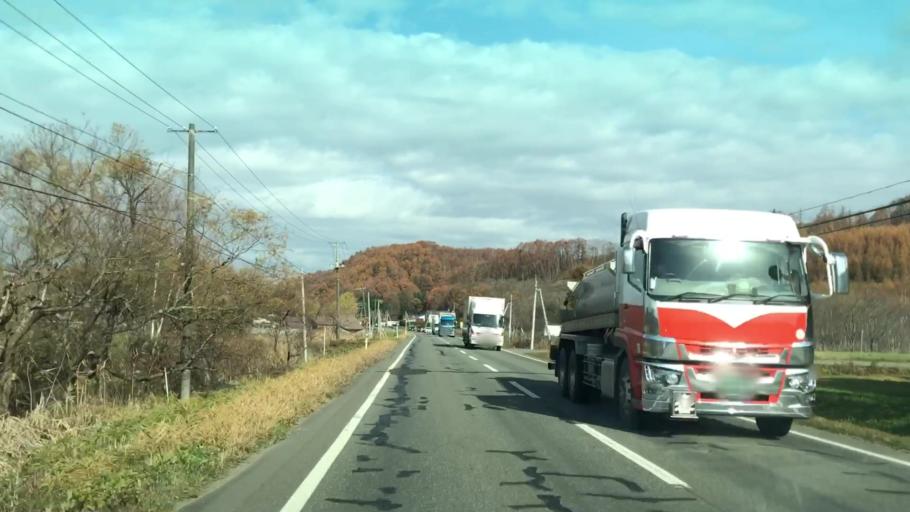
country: JP
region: Hokkaido
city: Shizunai-furukawacho
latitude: 42.6144
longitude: 142.1489
